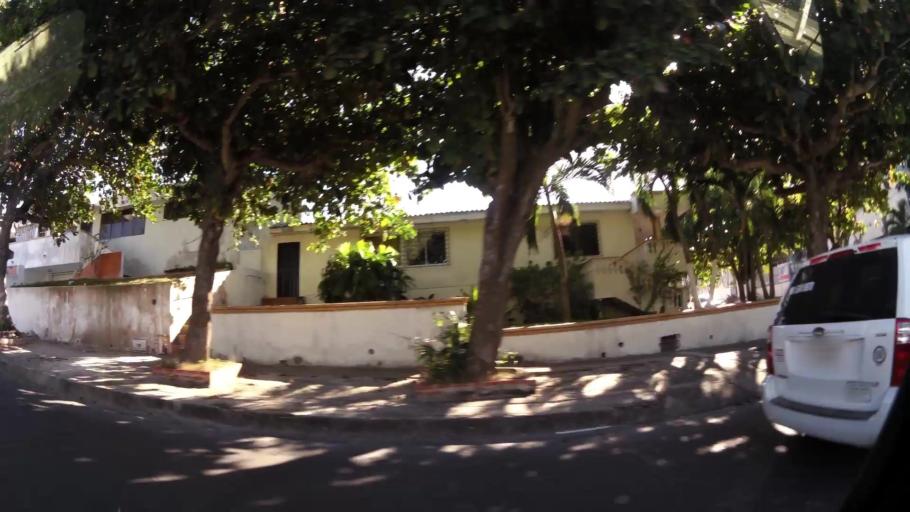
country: CO
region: Atlantico
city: Barranquilla
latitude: 10.9984
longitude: -74.8247
